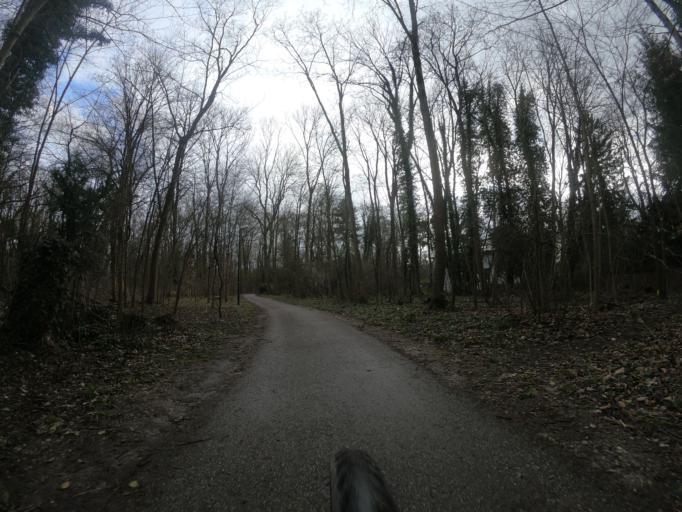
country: DE
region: Bavaria
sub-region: Upper Bavaria
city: Fuerstenfeldbruck
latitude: 48.1809
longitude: 11.2689
